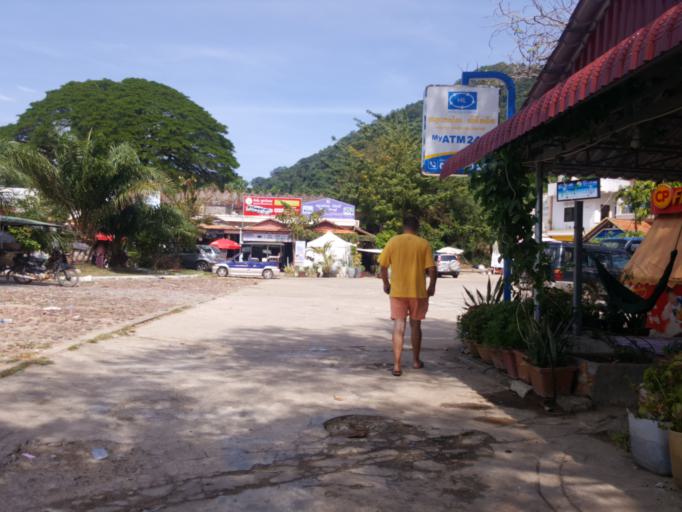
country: KH
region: Kep
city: Krong Kep
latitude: 10.4796
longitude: 104.2939
